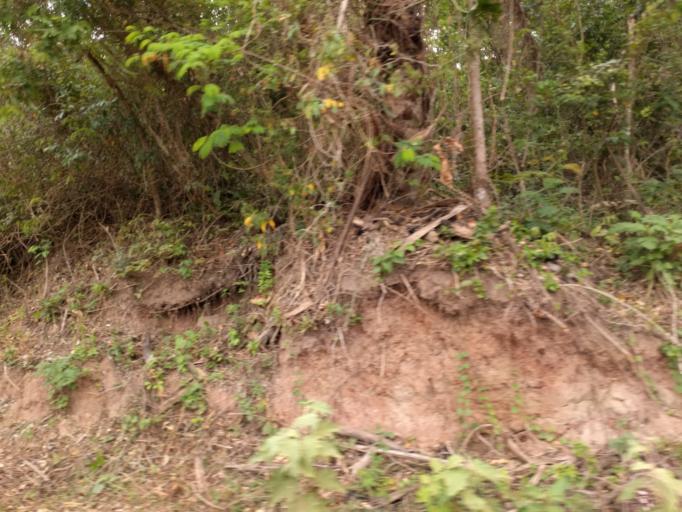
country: BO
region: Santa Cruz
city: Santiago del Torno
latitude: -17.9123
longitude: -63.4362
